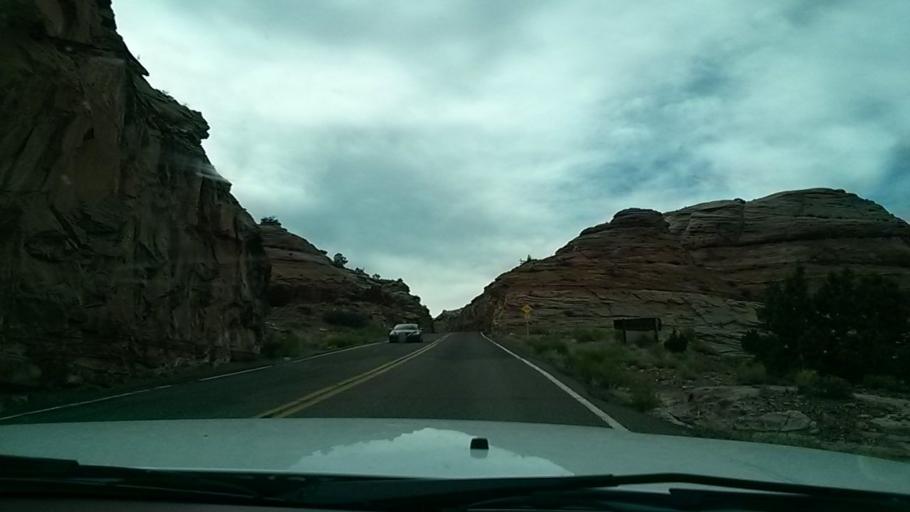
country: US
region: Utah
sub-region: Wayne County
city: Loa
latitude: 37.7718
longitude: -111.4187
